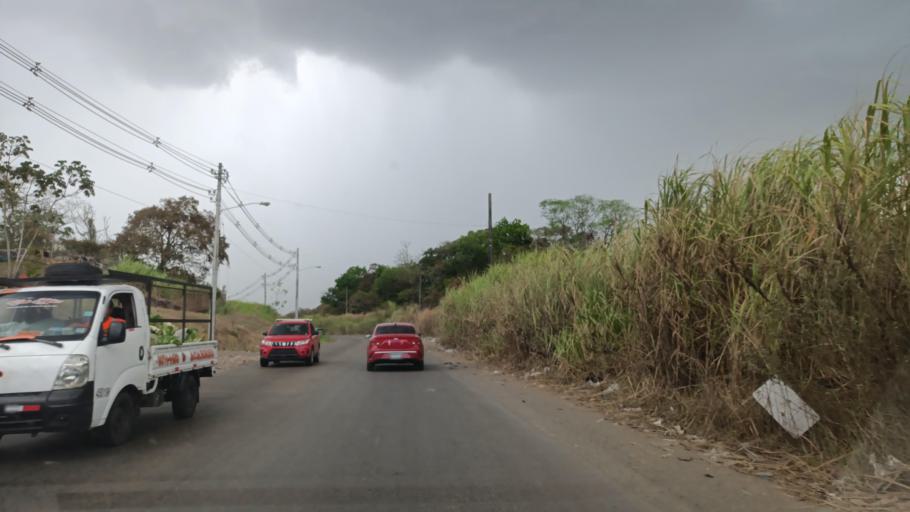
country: PA
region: Panama
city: Las Cumbres
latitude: 9.0439
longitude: -79.5639
